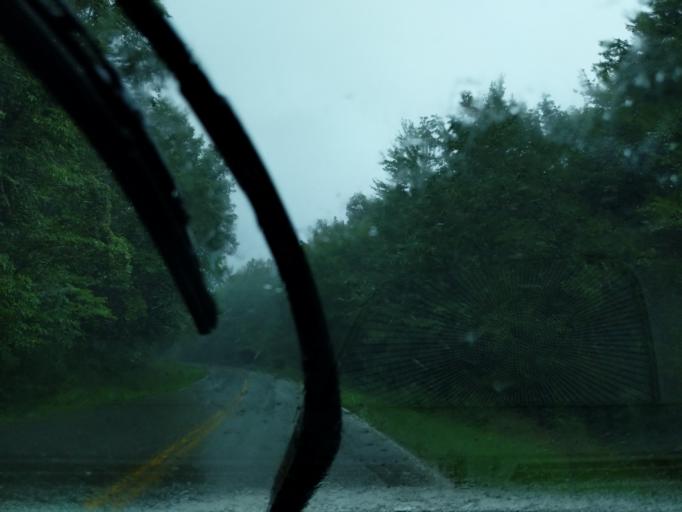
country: US
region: Kentucky
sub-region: Barren County
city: Cave City
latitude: 37.1382
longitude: -86.0736
